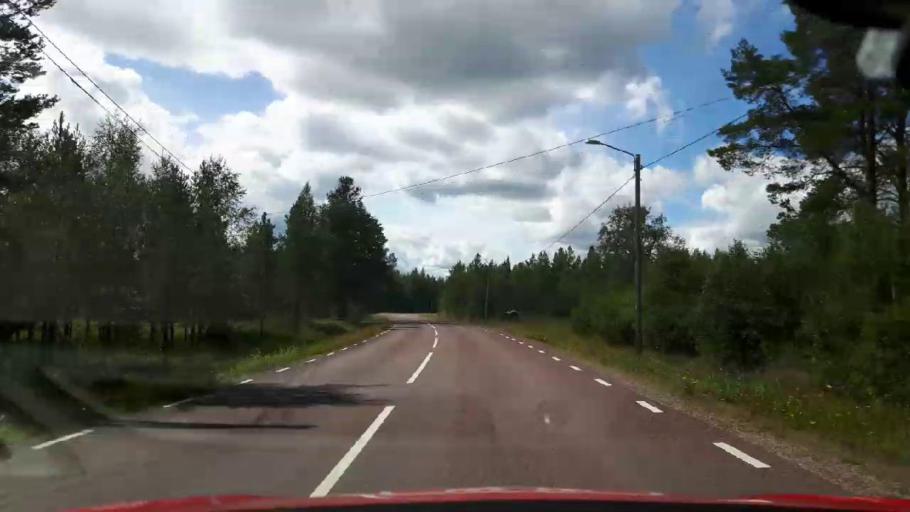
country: SE
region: Jaemtland
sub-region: Harjedalens Kommun
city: Sveg
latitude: 61.8627
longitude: 14.1107
